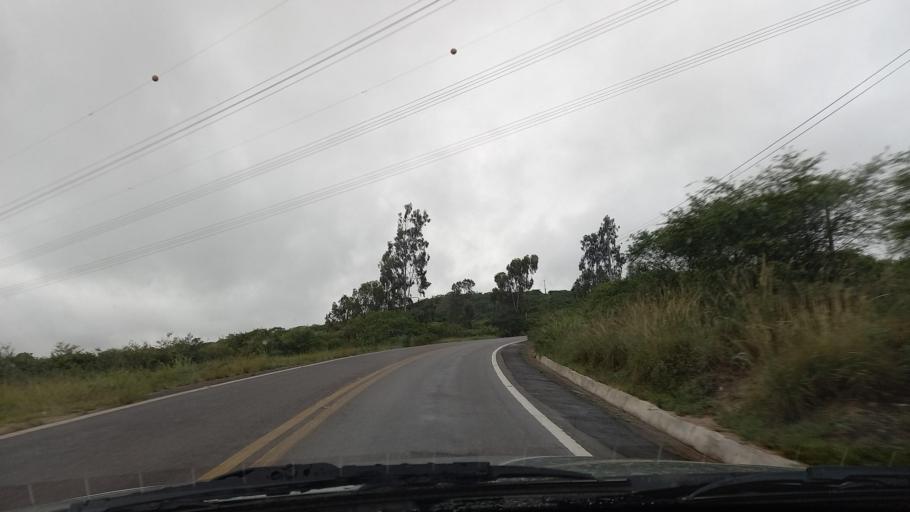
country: BR
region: Pernambuco
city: Garanhuns
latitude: -8.8496
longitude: -36.5160
